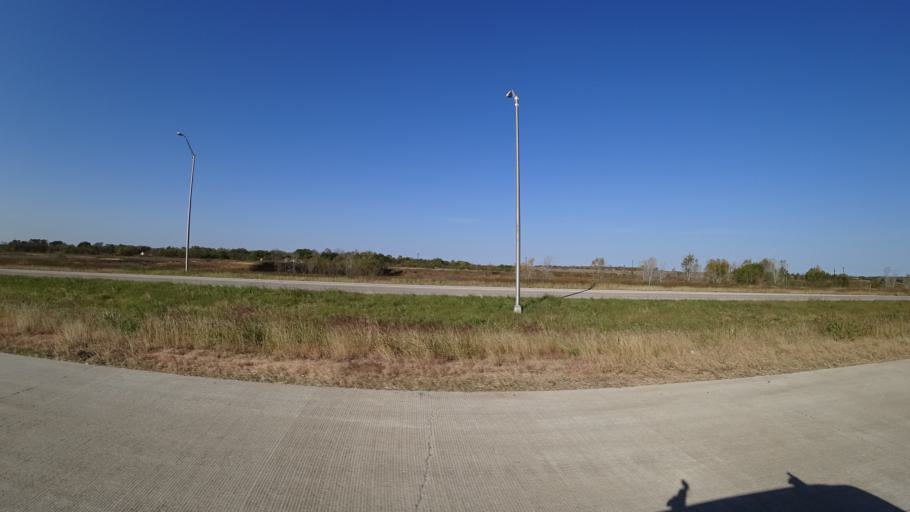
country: US
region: Texas
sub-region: Travis County
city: Hornsby Bend
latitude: 30.2253
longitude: -97.6225
